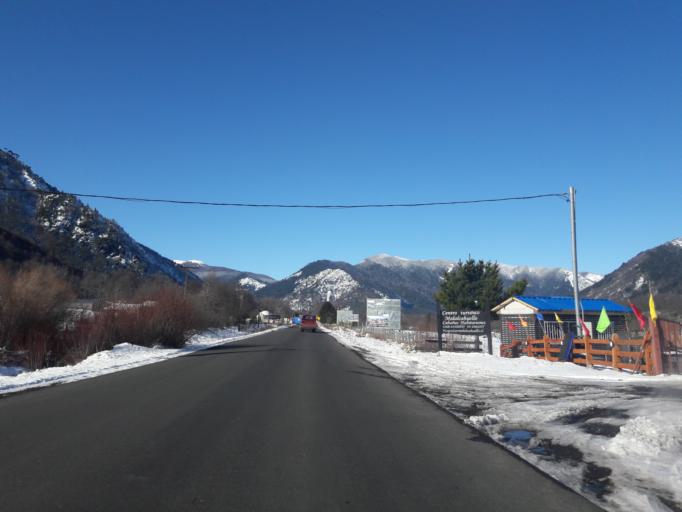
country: CL
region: Araucania
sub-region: Provincia de Cautin
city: Vilcun
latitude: -38.4719
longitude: -71.5684
